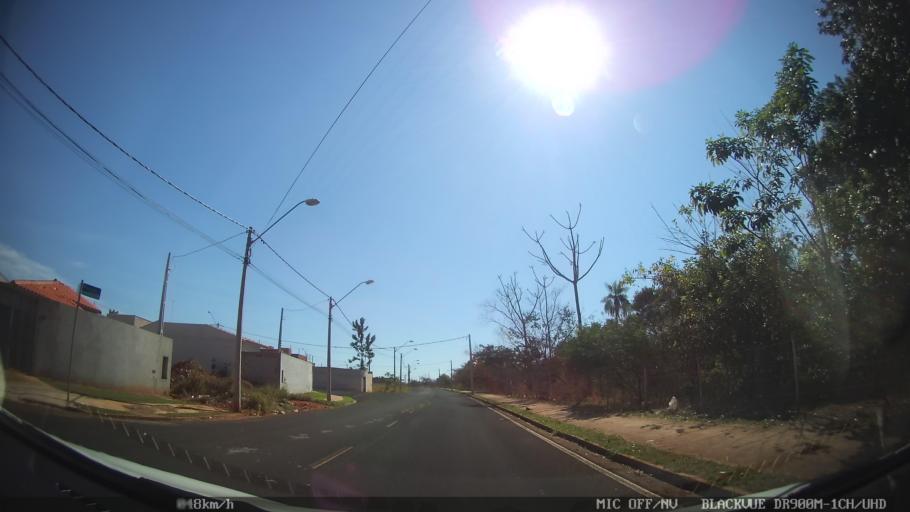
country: BR
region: Sao Paulo
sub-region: Sao Jose Do Rio Preto
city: Sao Jose do Rio Preto
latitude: -20.7575
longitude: -49.4208
